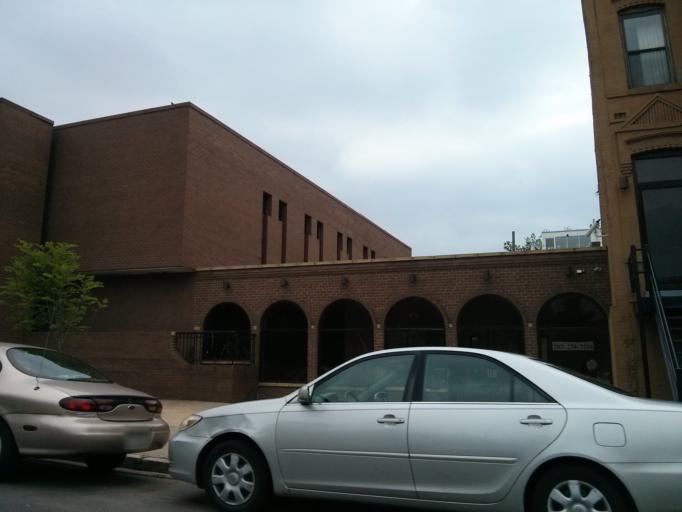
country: US
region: Washington, D.C.
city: Washington, D.C.
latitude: 38.9091
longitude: -77.0199
